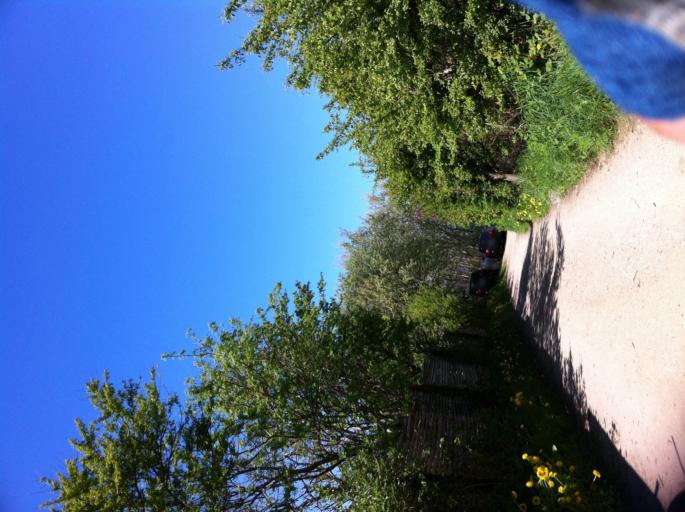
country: DK
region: Capital Region
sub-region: Halsnaes Kommune
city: Hundested
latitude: 55.9739
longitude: 11.8532
